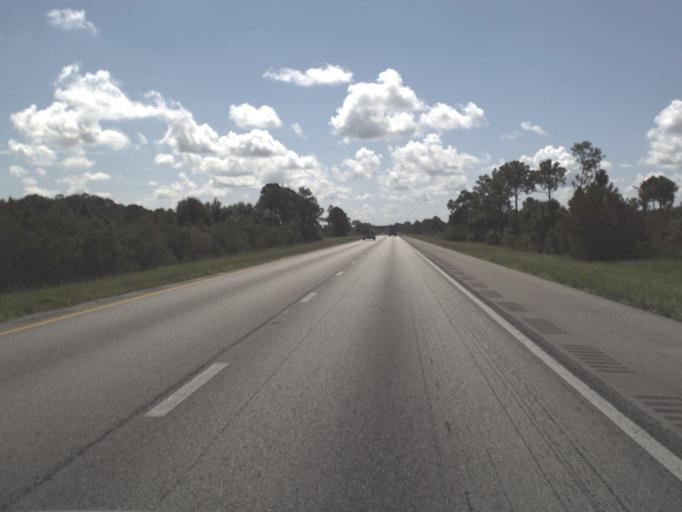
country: US
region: Florida
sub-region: Lee County
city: Burnt Store Marina
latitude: 26.8172
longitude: -81.9397
